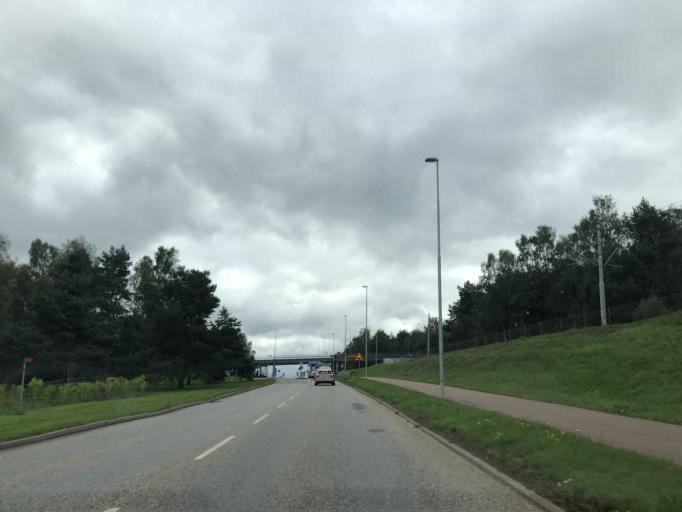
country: SE
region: Vaestra Goetaland
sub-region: Goteborg
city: Majorna
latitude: 57.7342
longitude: 11.8962
